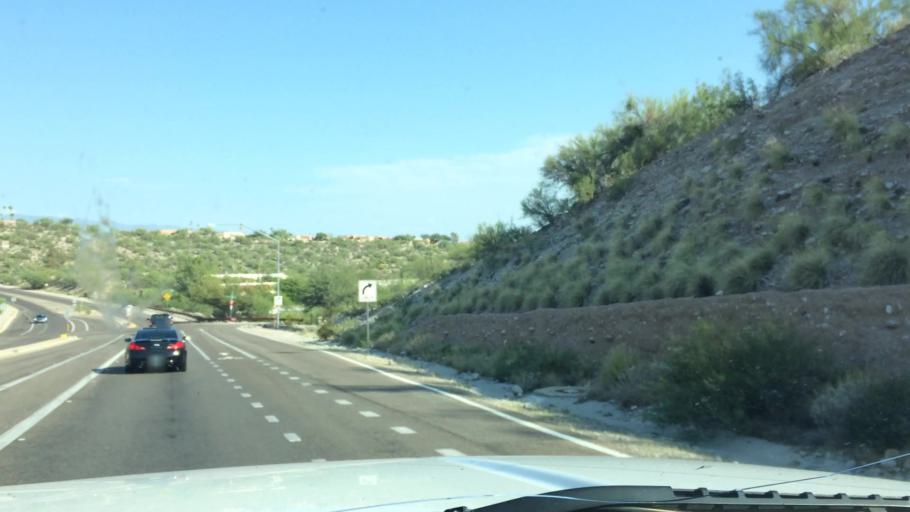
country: US
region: Arizona
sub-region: Pima County
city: Catalina Foothills
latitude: 32.3074
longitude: -110.8708
